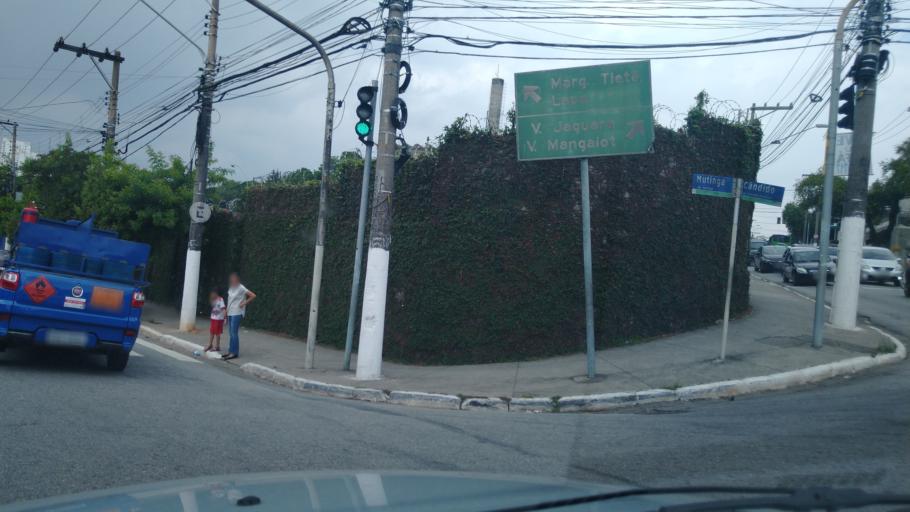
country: BR
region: Sao Paulo
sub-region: Osasco
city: Osasco
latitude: -23.5056
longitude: -46.7592
